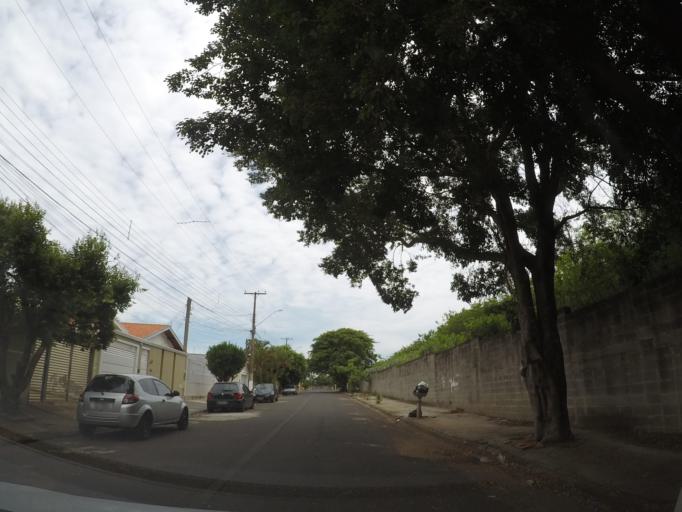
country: BR
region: Sao Paulo
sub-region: Hortolandia
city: Hortolandia
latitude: -22.8351
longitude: -47.1909
